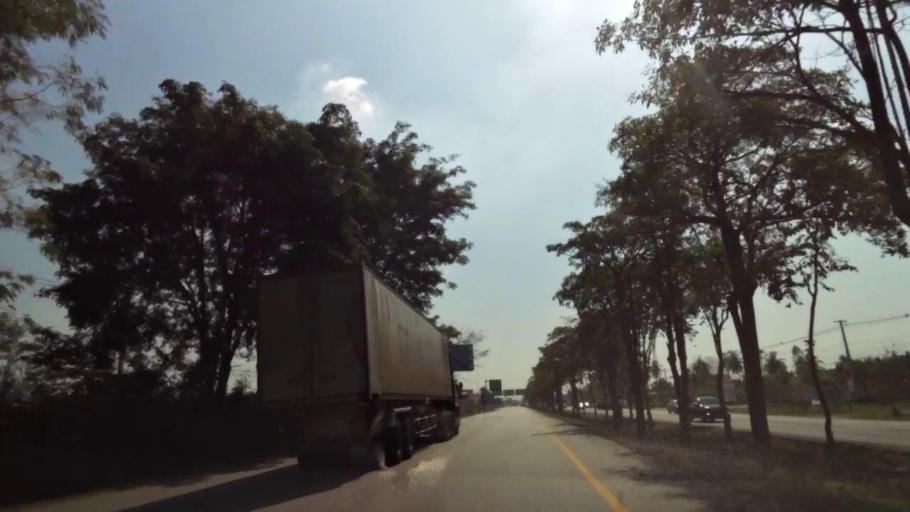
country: TH
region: Phichit
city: Bueng Na Rang
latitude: 16.1307
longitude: 100.1255
